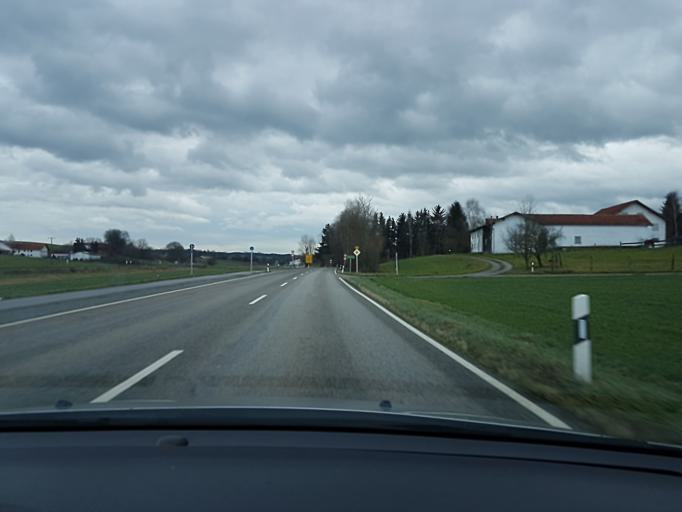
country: DE
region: Bavaria
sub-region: Upper Bavaria
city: Neumarkt-Sankt Veit
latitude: 48.3690
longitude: 12.4902
